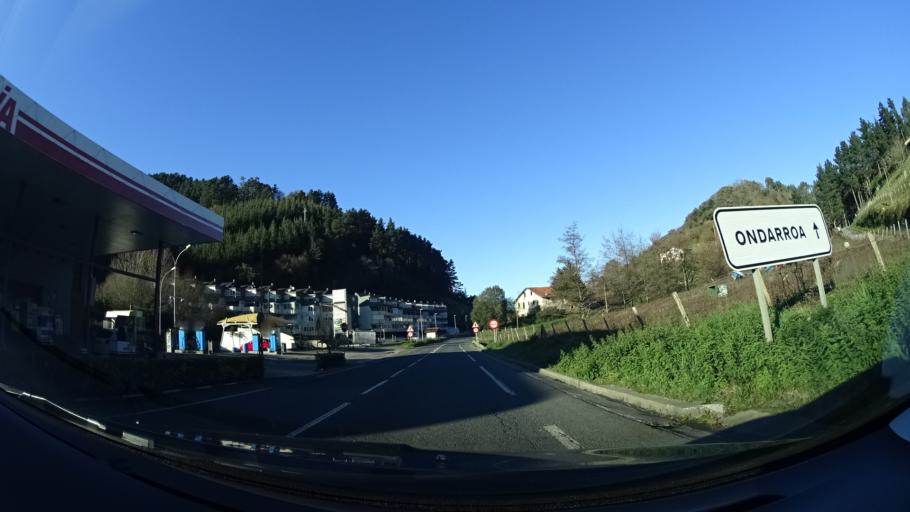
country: ES
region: Basque Country
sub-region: Bizkaia
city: Ondarroa
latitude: 43.3138
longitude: -2.4109
